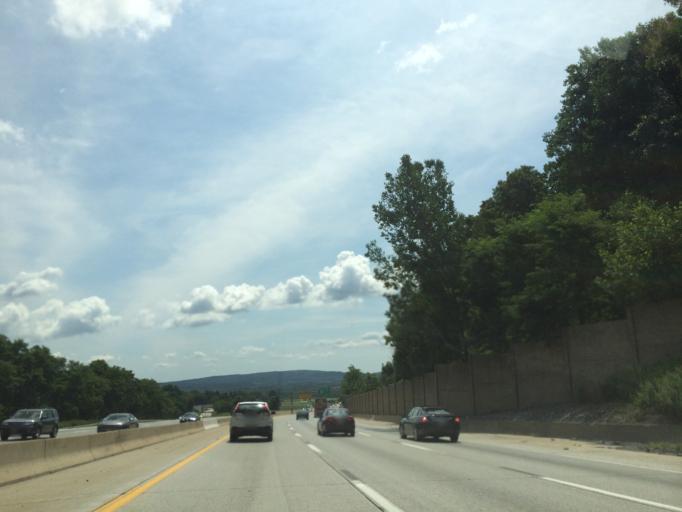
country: US
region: Pennsylvania
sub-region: Lehigh County
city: Emmaus
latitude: 40.5591
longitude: -75.4450
